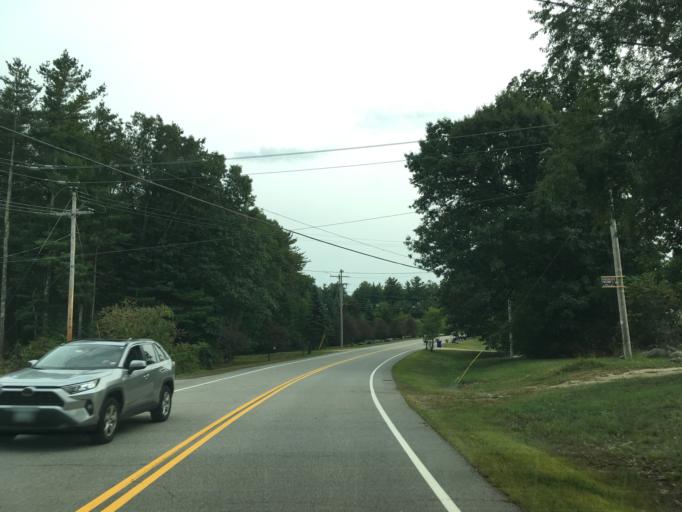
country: US
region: New Hampshire
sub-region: Rockingham County
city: Exeter
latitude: 42.9795
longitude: -70.9066
